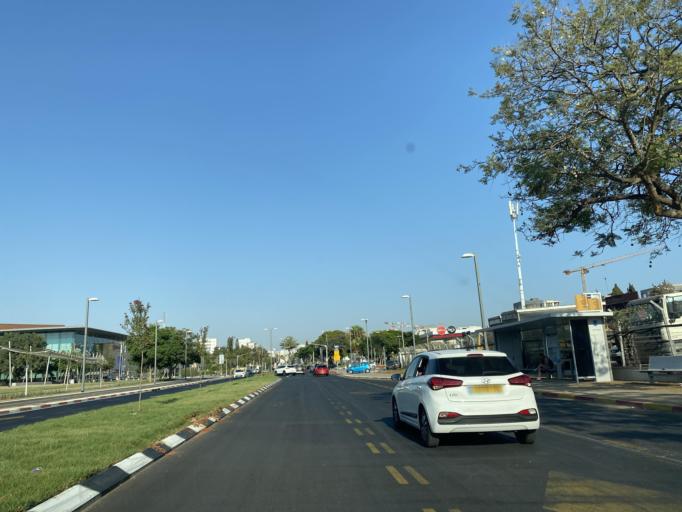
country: IL
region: Tel Aviv
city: Herzliyya
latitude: 32.1642
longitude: 34.8215
